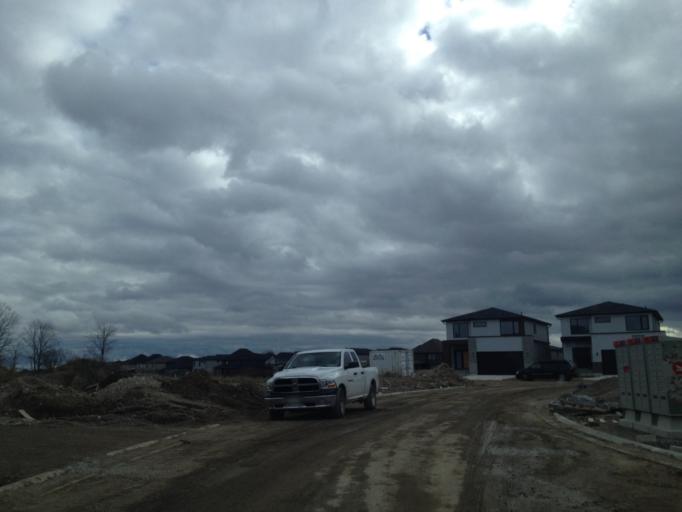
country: CA
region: Ontario
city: London
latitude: 43.0198
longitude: -81.3327
